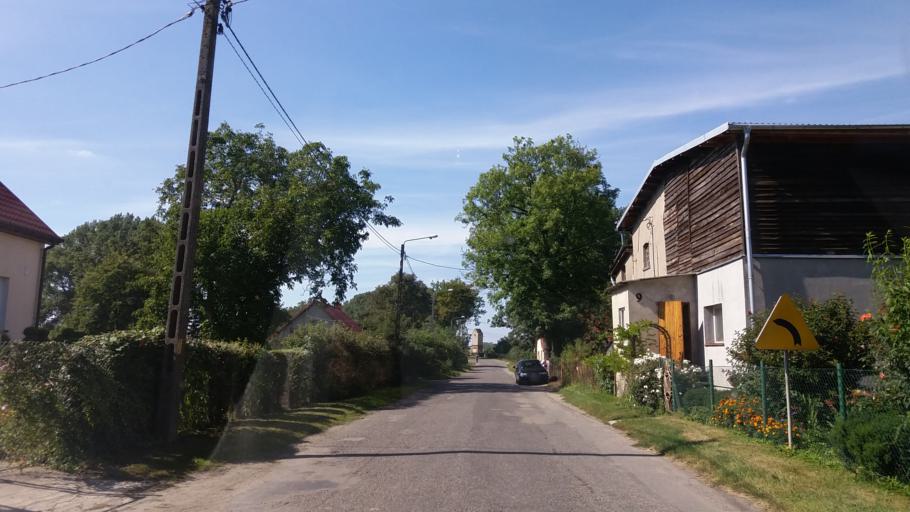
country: PL
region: West Pomeranian Voivodeship
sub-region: Powiat choszczenski
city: Choszczno
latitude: 53.1289
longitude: 15.4094
